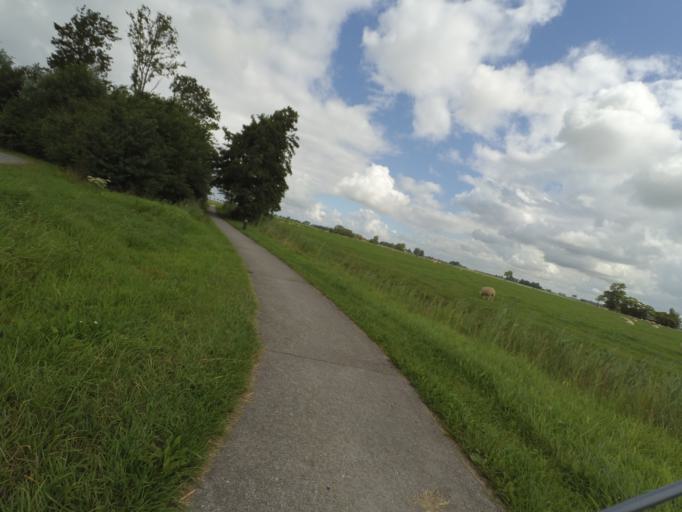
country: NL
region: Friesland
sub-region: Gemeente Kollumerland en Nieuwkruisland
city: Kollum
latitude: 53.2817
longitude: 6.2215
